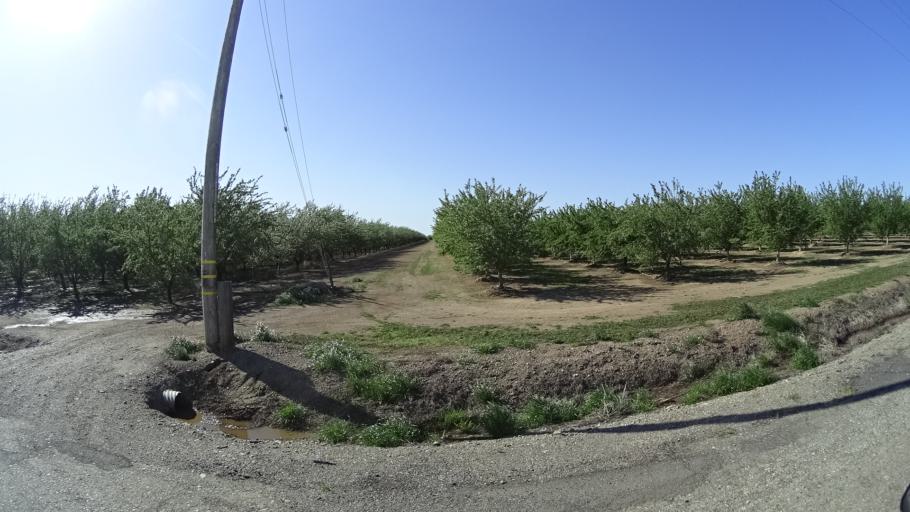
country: US
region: California
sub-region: Glenn County
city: Hamilton City
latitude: 39.7756
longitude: -122.0523
